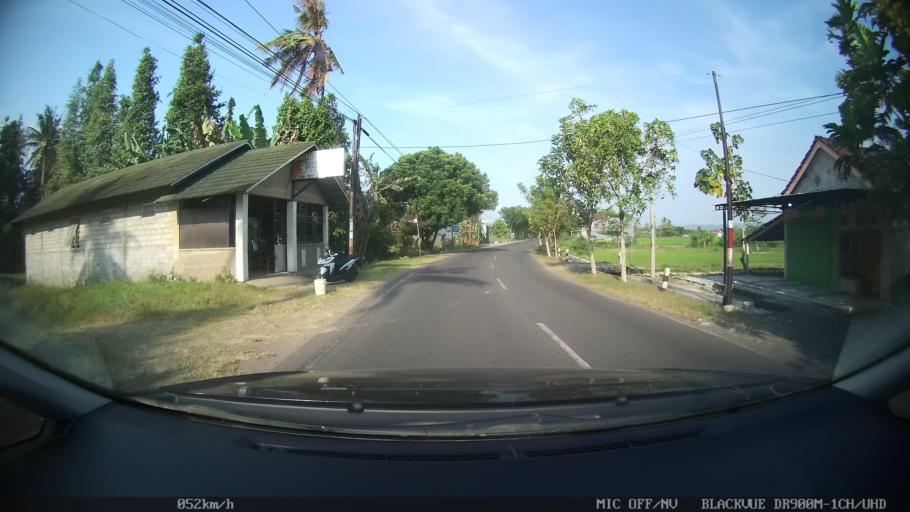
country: ID
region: Daerah Istimewa Yogyakarta
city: Pandak
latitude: -7.9017
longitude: 110.3030
